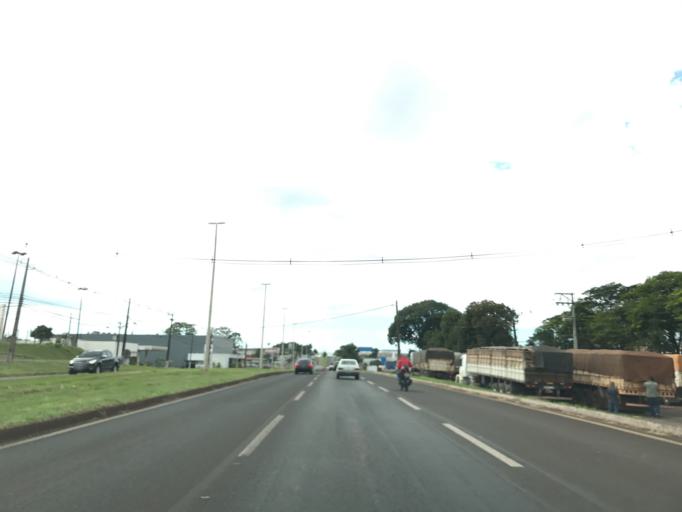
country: BR
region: Parana
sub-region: Cambe
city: Cambe
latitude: -23.2822
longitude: -51.2526
